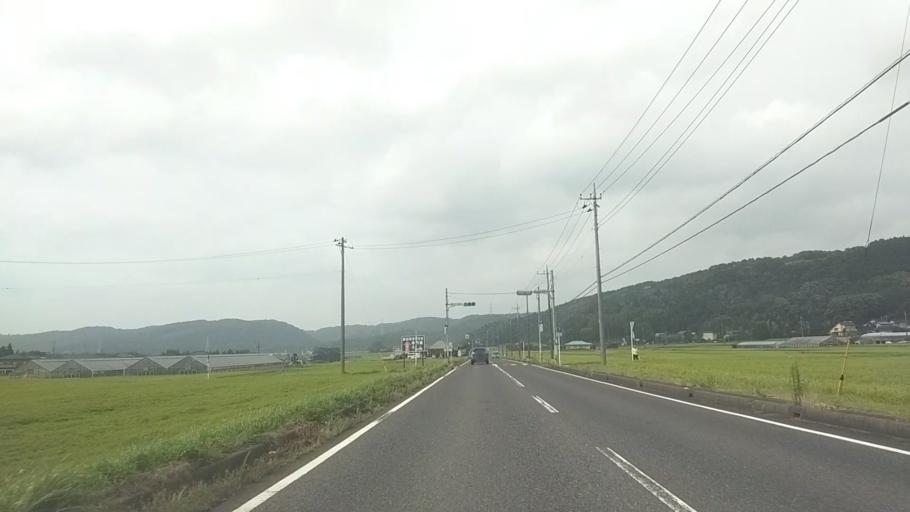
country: JP
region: Chiba
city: Kimitsu
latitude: 35.2889
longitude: 139.9903
